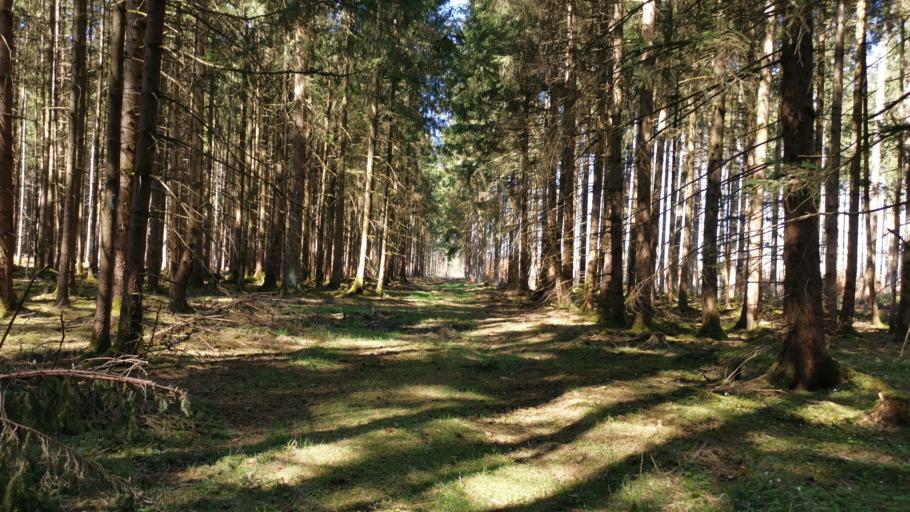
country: DE
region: Bavaria
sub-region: Upper Bavaria
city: Pullach im Isartal
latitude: 48.0686
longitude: 11.4909
